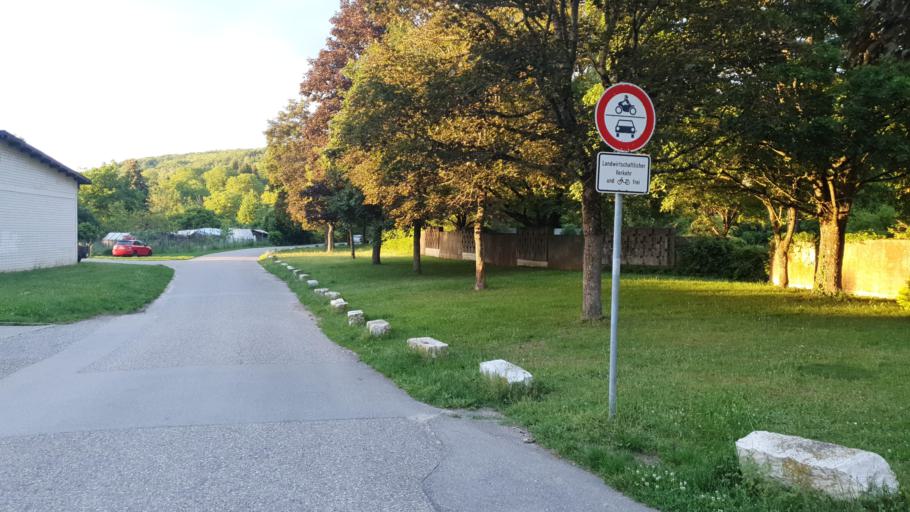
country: DE
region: Baden-Wuerttemberg
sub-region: Freiburg Region
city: Weil am Rhein
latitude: 47.5992
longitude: 7.6263
